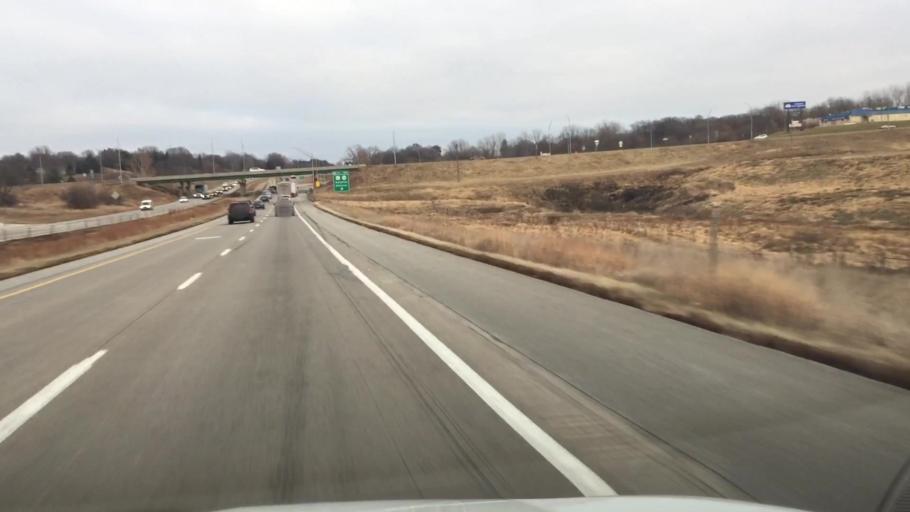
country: US
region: Iowa
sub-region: Jasper County
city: Newton
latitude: 41.6826
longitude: -93.0802
